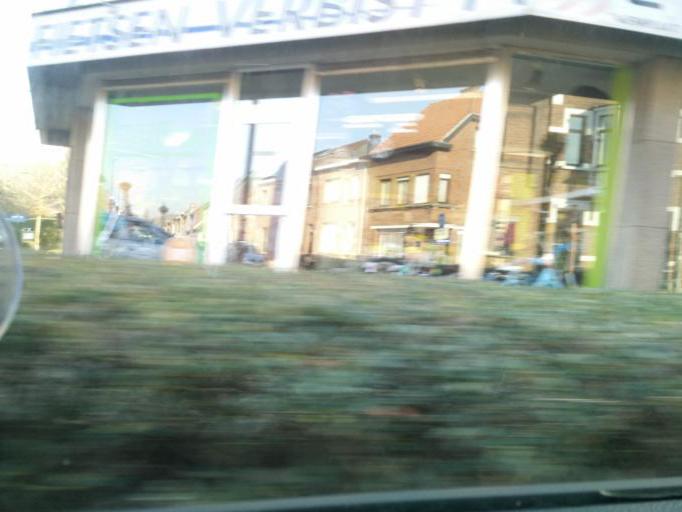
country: BE
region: Flanders
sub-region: Provincie Antwerpen
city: Kapellen
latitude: 51.3078
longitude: 4.4091
